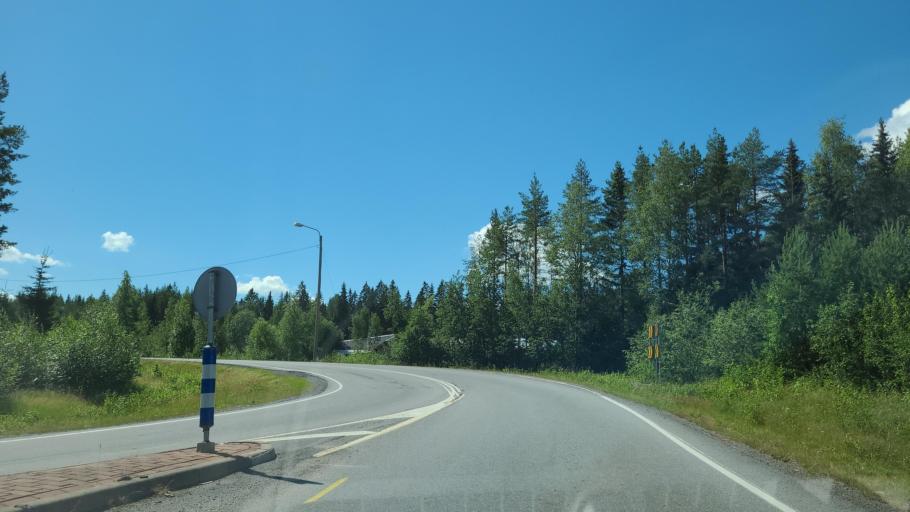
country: FI
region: Southern Ostrobothnia
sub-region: Seinaejoki
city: Seinaejoki
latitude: 62.8411
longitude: 22.7974
